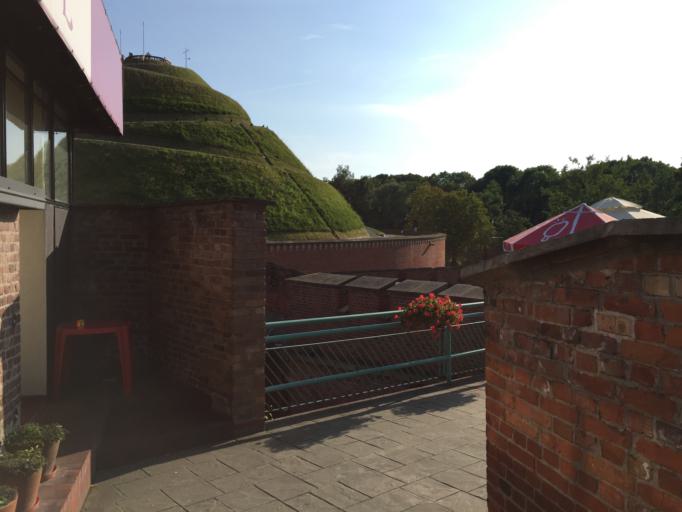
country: PL
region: Lesser Poland Voivodeship
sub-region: Krakow
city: Krakow
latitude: 50.0557
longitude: 19.8941
